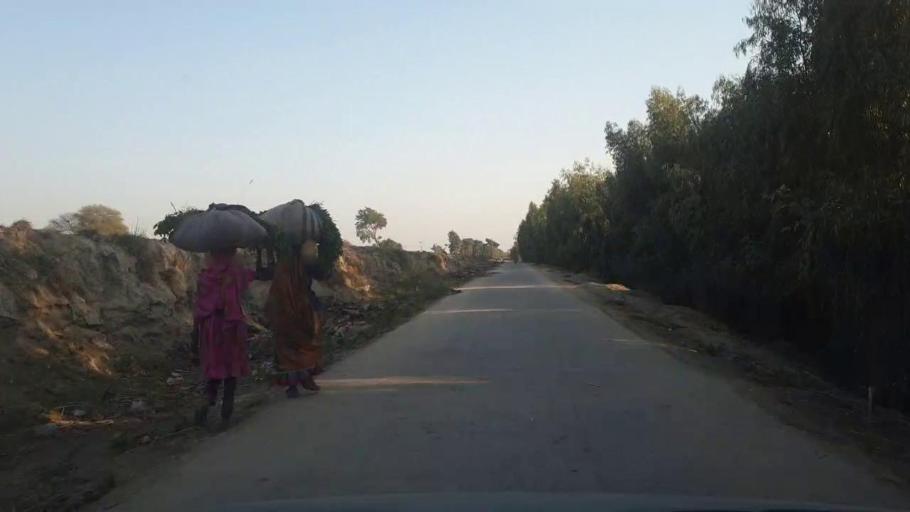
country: PK
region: Sindh
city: Chambar
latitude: 25.2913
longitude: 68.8946
